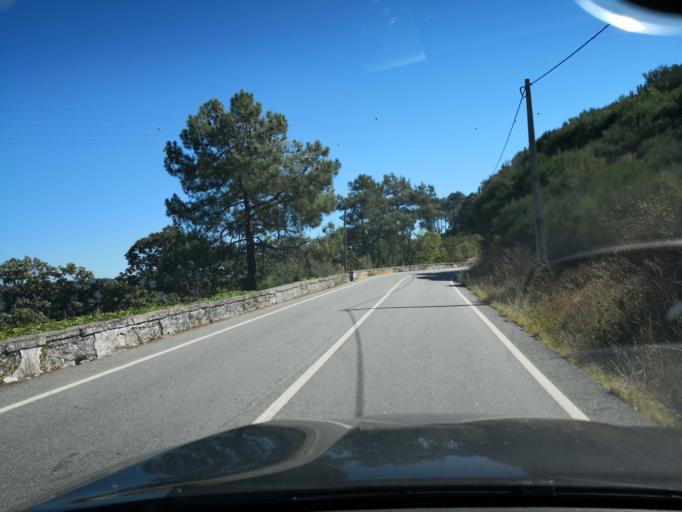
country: PT
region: Vila Real
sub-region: Vila Real
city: Vila Real
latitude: 41.2677
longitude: -7.7792
